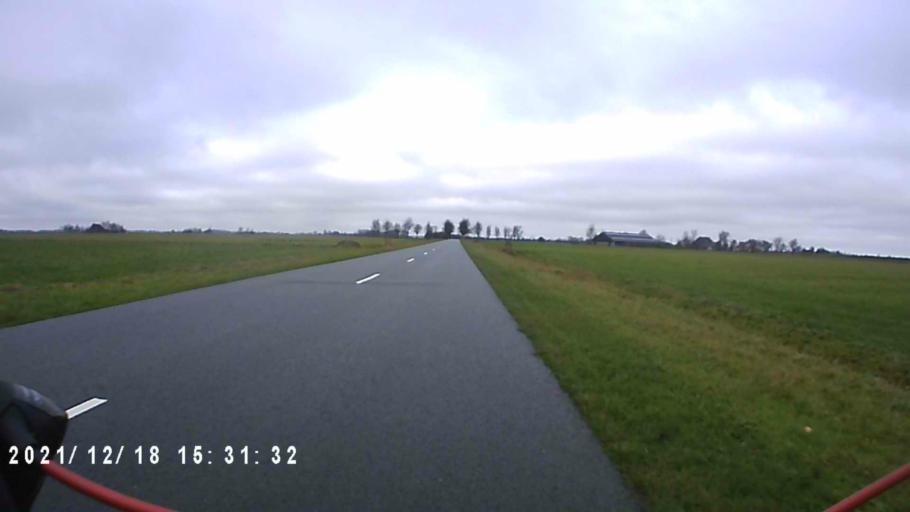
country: NL
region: Friesland
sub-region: Gemeente Dongeradeel
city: Anjum
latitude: 53.3396
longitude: 6.1366
